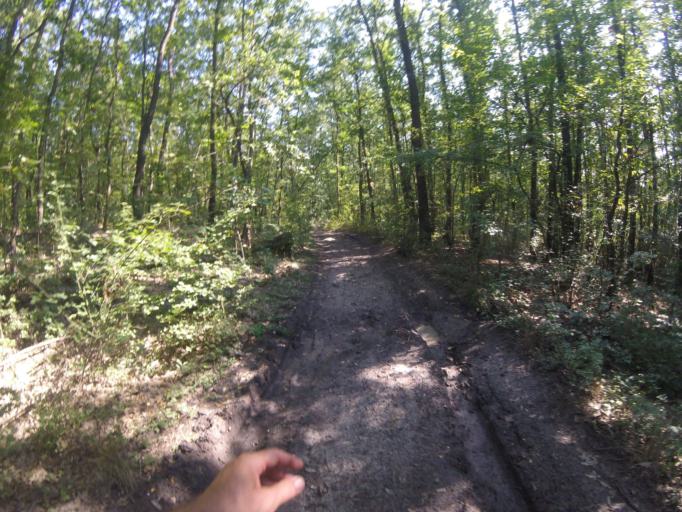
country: HU
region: Nograd
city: Bujak
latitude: 47.8932
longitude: 19.5386
